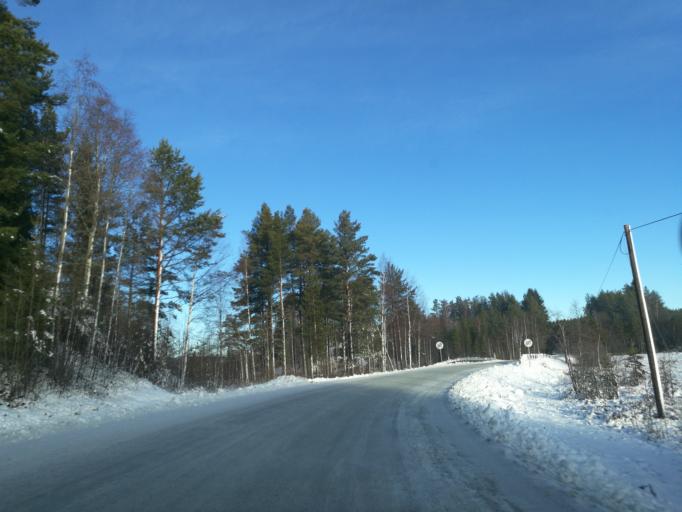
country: NO
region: Hedmark
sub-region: Grue
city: Kirkenaer
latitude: 60.3609
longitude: 12.3474
